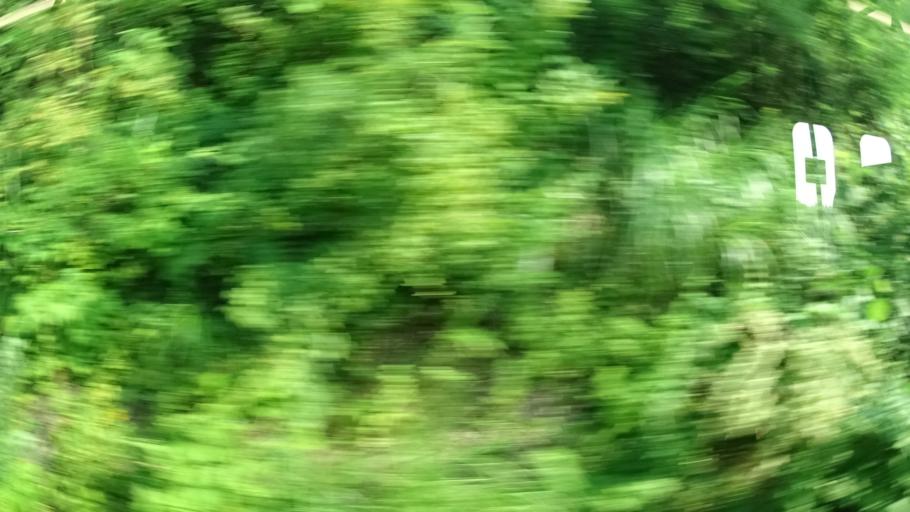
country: JP
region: Fukushima
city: Iwaki
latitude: 36.9391
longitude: 140.8072
